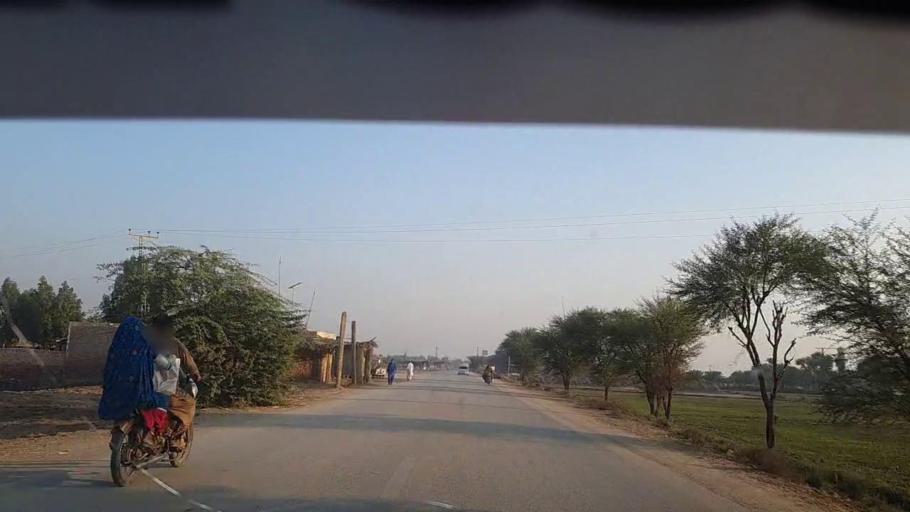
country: PK
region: Sindh
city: Ranipur
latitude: 27.2664
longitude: 68.5212
